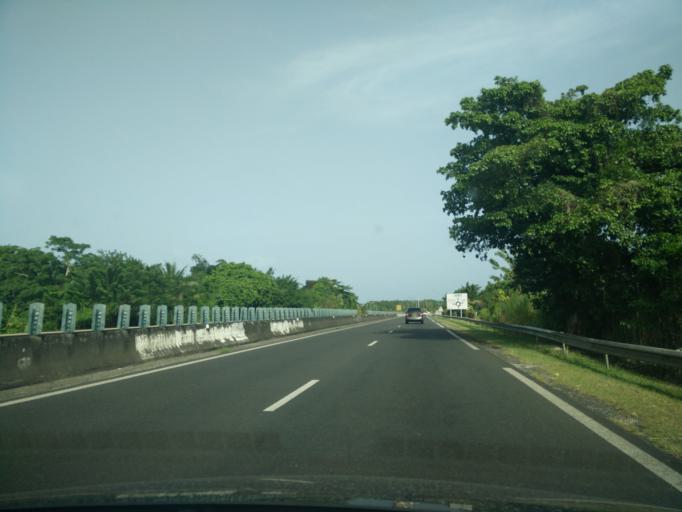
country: GP
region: Guadeloupe
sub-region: Guadeloupe
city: Petit-Bourg
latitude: 16.1754
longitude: -61.5913
